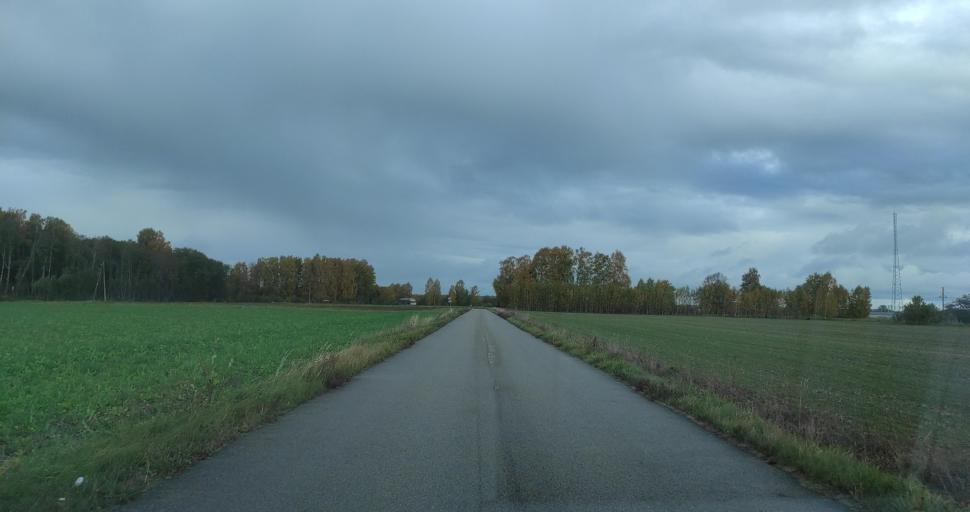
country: LV
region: Skrunda
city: Skrunda
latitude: 56.6902
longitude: 22.0190
